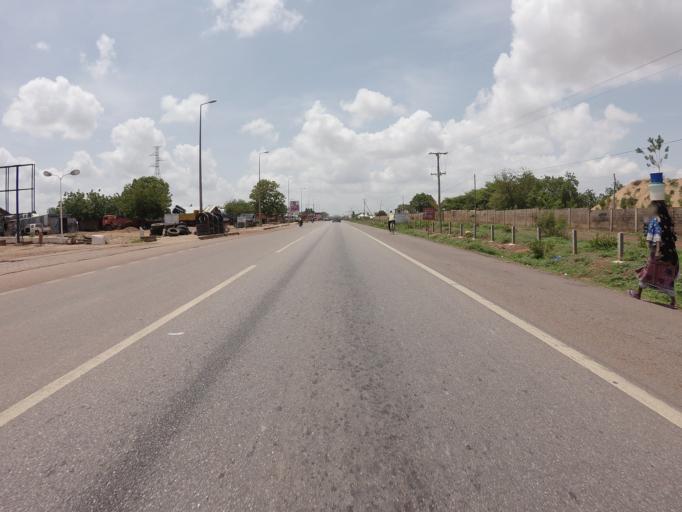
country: GH
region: Northern
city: Tamale
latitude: 9.3738
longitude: -0.8742
